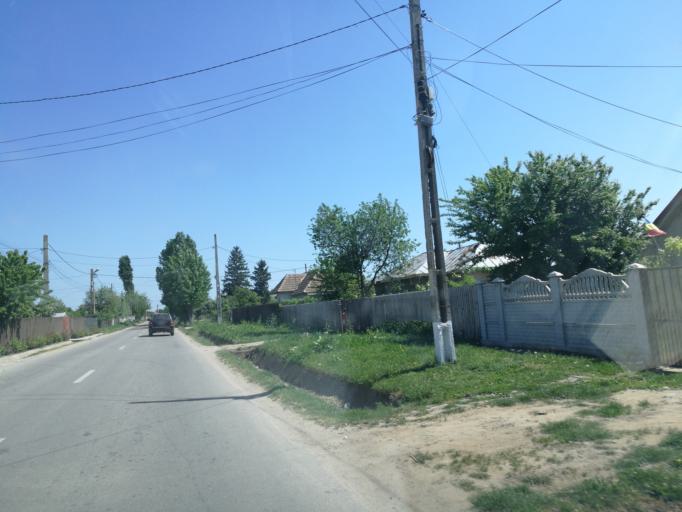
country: RO
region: Ialomita
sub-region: Comuna Maia
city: Maia
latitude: 44.7422
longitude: 26.4052
